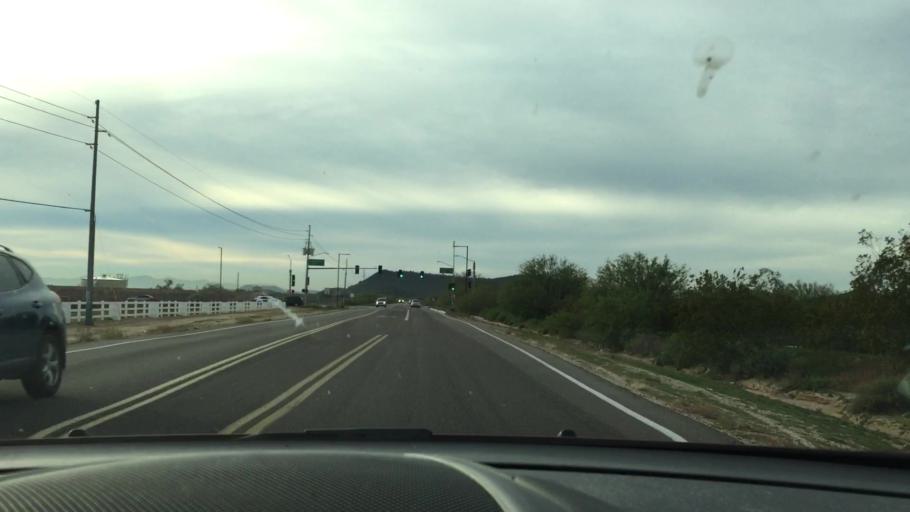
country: US
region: Arizona
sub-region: Maricopa County
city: Cave Creek
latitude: 33.6988
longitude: -112.0039
